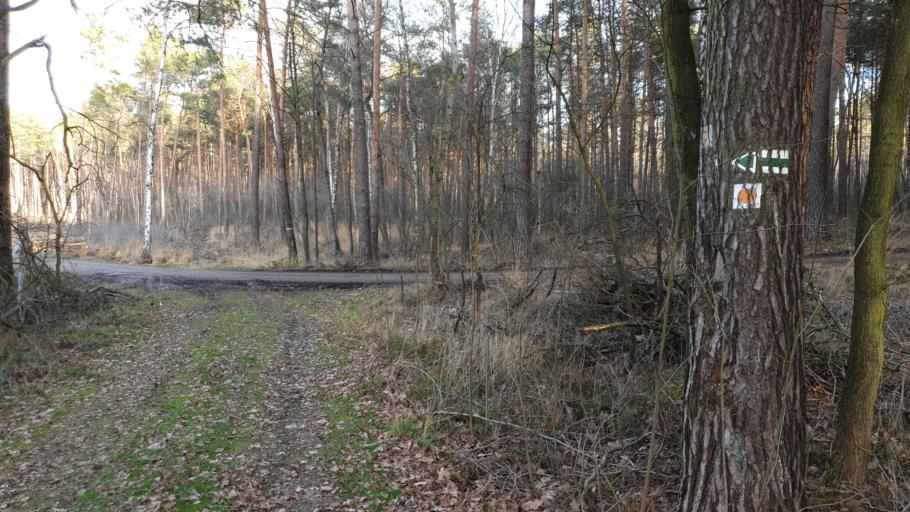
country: DE
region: Saxony
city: Schildau
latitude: 51.4447
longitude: 12.8936
